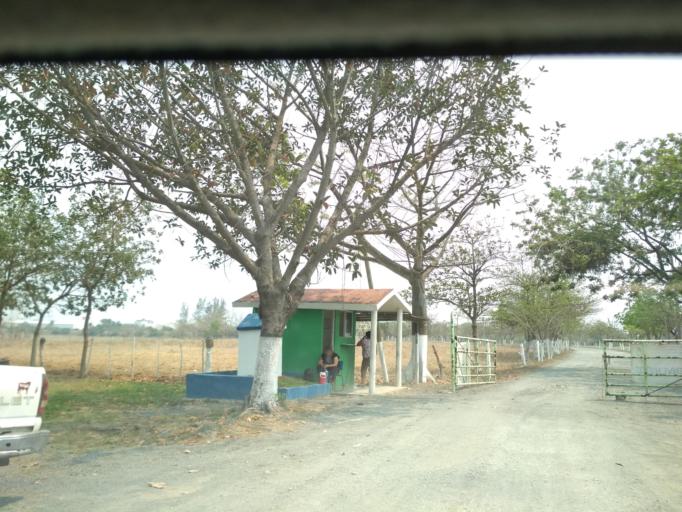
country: MX
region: Veracruz
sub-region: Veracruz
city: Las Amapolas
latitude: 19.1675
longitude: -96.2085
